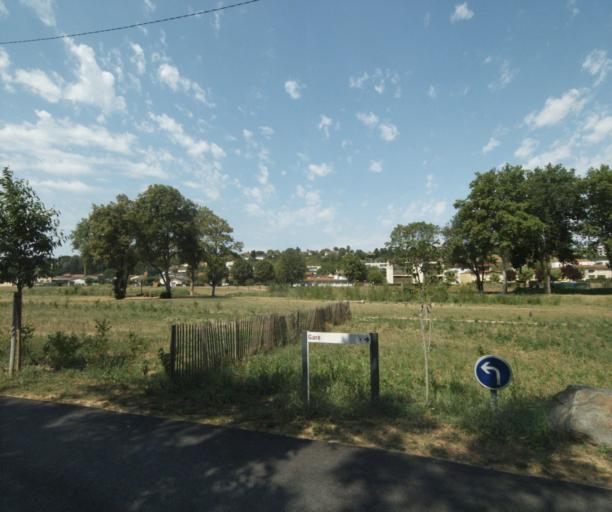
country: FR
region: Rhone-Alpes
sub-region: Departement du Rhone
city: Saint-Germain-Nuelles
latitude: 45.8296
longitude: 4.6160
